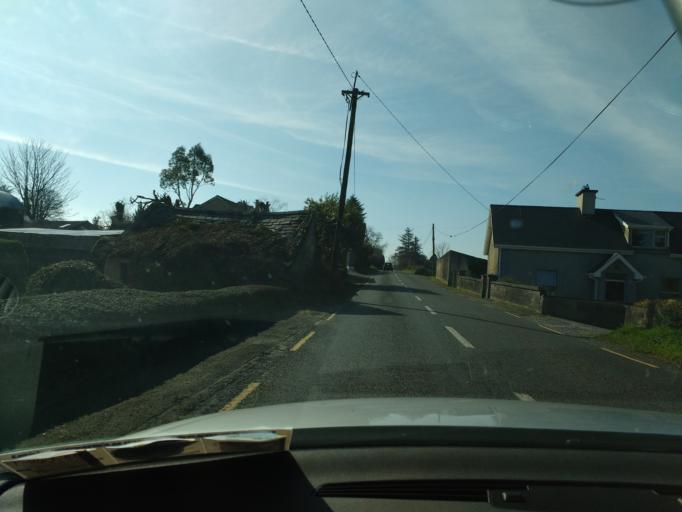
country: IE
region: Munster
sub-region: County Limerick
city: Castleconnell
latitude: 52.6882
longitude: -8.4820
